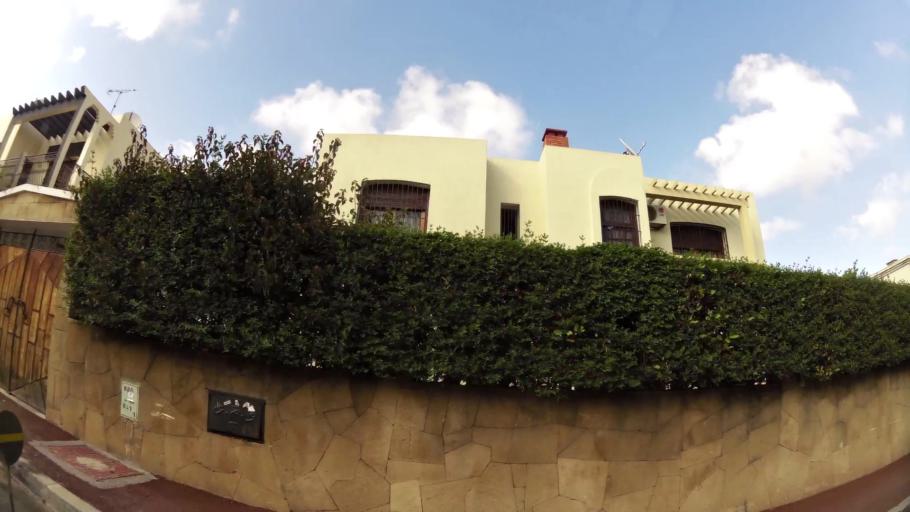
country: MA
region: Rabat-Sale-Zemmour-Zaer
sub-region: Skhirate-Temara
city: Temara
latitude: 33.9509
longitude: -6.8656
